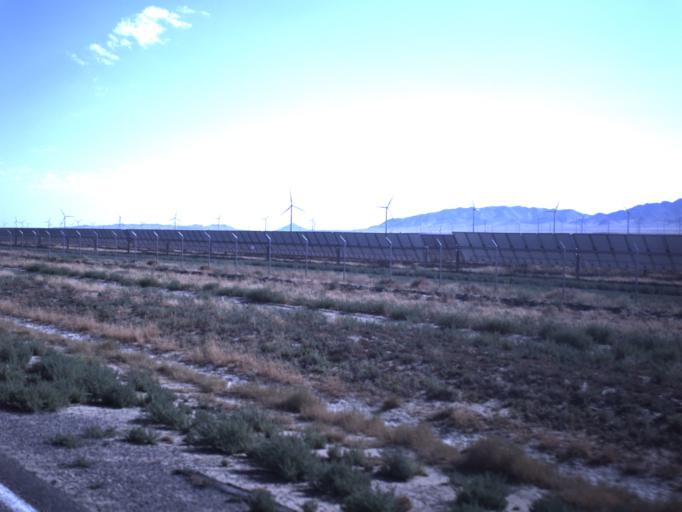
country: US
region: Utah
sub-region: Beaver County
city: Milford
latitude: 38.4896
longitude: -112.9911
